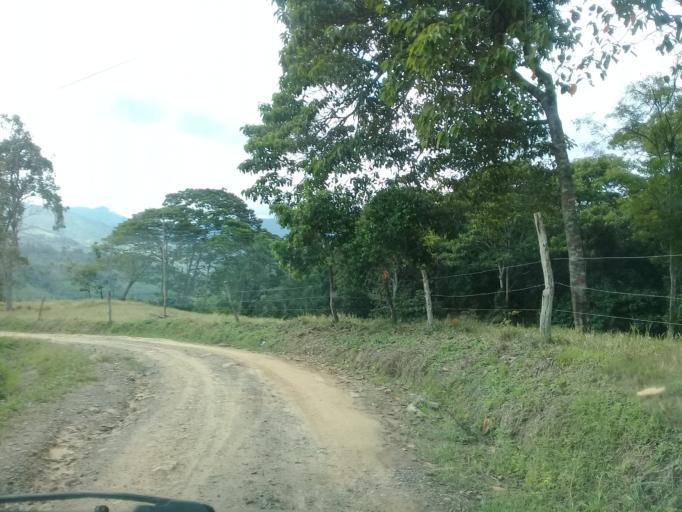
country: CO
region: Cundinamarca
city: Chaguani
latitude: 5.0054
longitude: -74.5863
